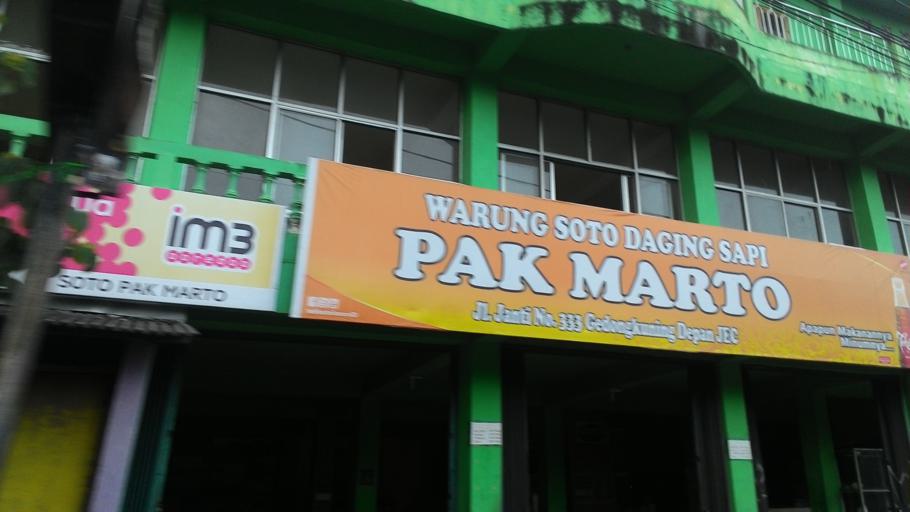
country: ID
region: Daerah Istimewa Yogyakarta
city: Yogyakarta
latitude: -7.7985
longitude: 110.4033
